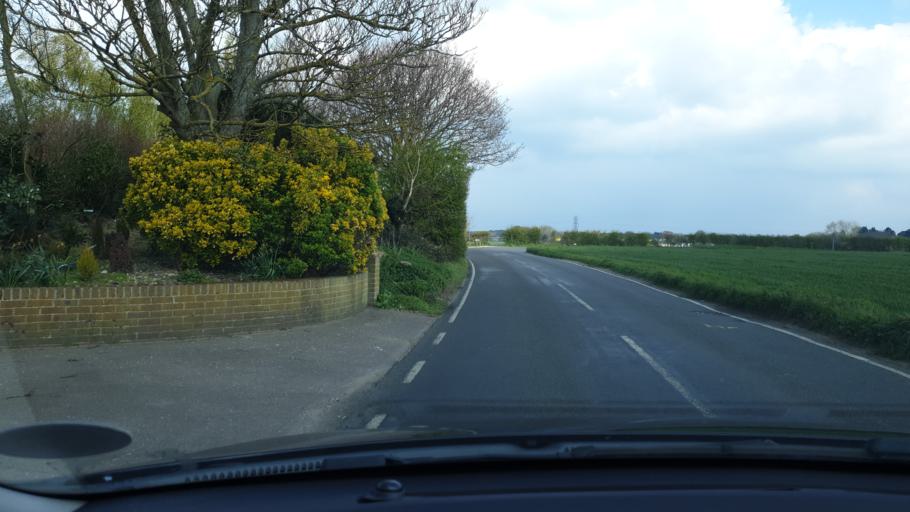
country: GB
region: England
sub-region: Essex
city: Great Bentley
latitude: 51.8694
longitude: 1.1038
